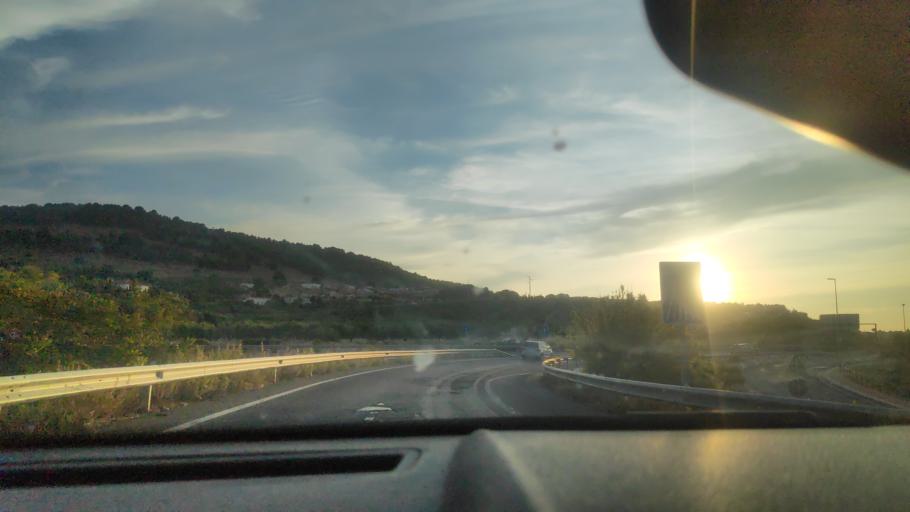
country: ES
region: Andalusia
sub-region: Provincia de Jaen
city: Jaen
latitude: 37.7885
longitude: -3.8317
